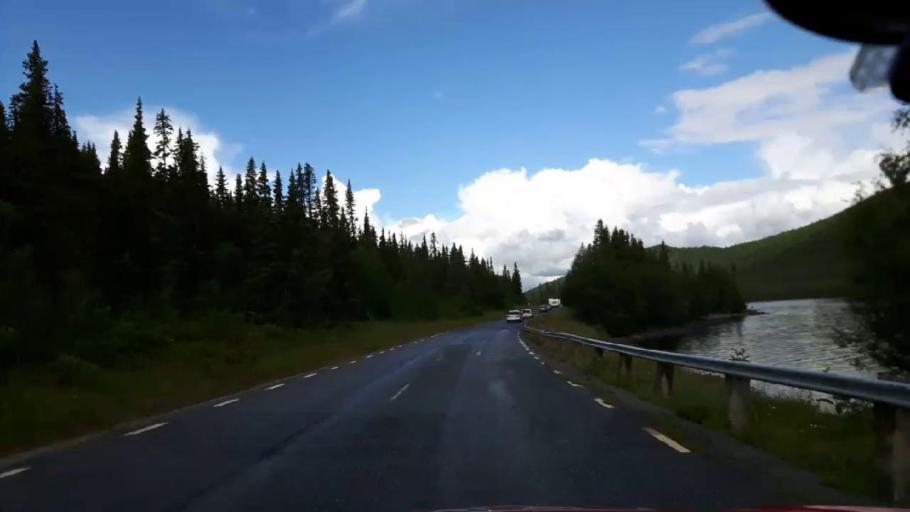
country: SE
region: Vaesterbotten
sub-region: Vilhelmina Kommun
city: Sjoberg
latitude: 65.0235
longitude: 15.1549
